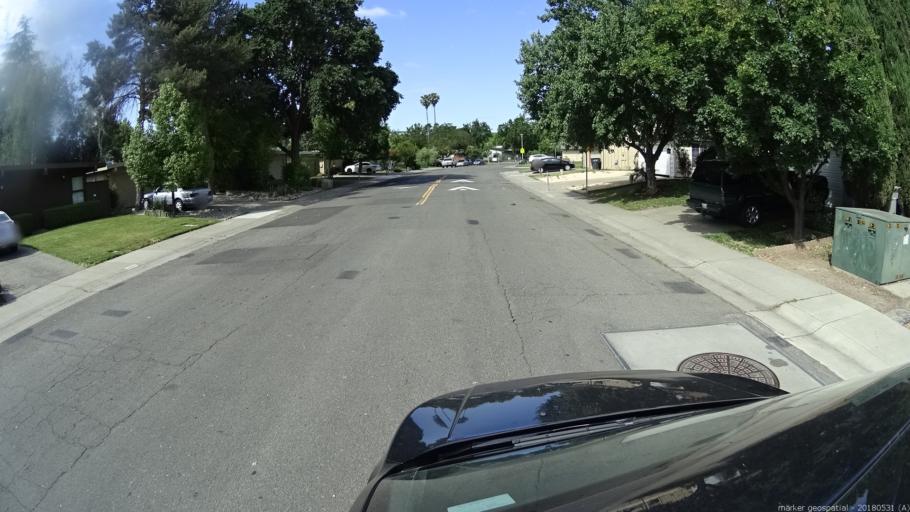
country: US
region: California
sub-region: Sacramento County
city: Sacramento
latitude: 38.6170
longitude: -121.5012
